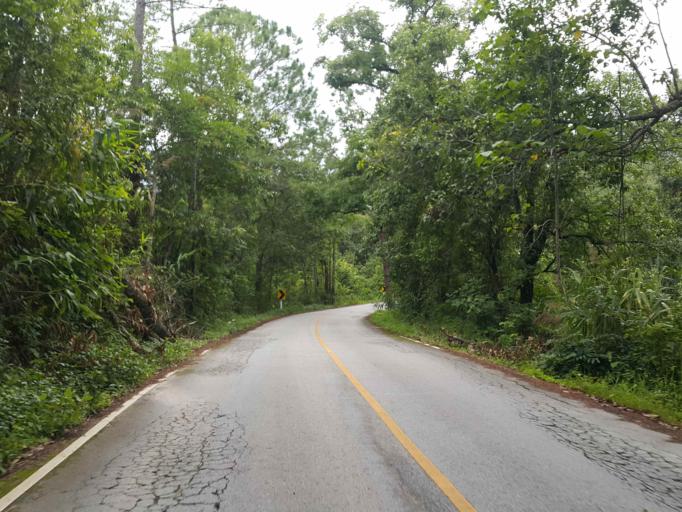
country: TH
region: Chiang Mai
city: Mae Chaem
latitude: 18.5128
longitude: 98.4578
